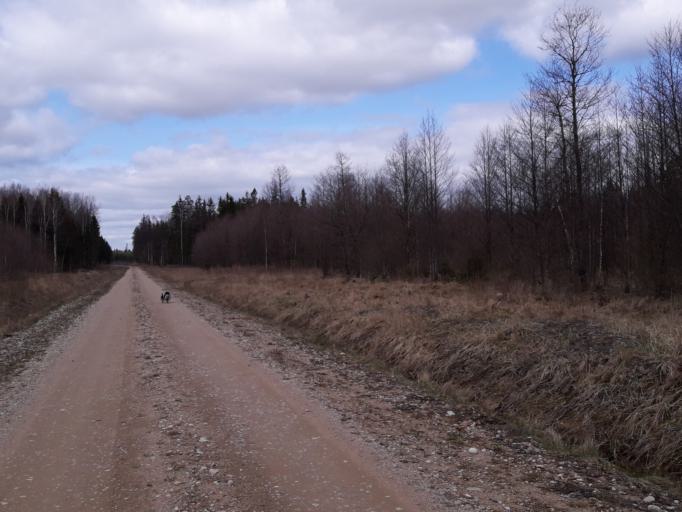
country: LV
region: Talsu Rajons
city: Sabile
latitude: 56.9000
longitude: 22.3776
